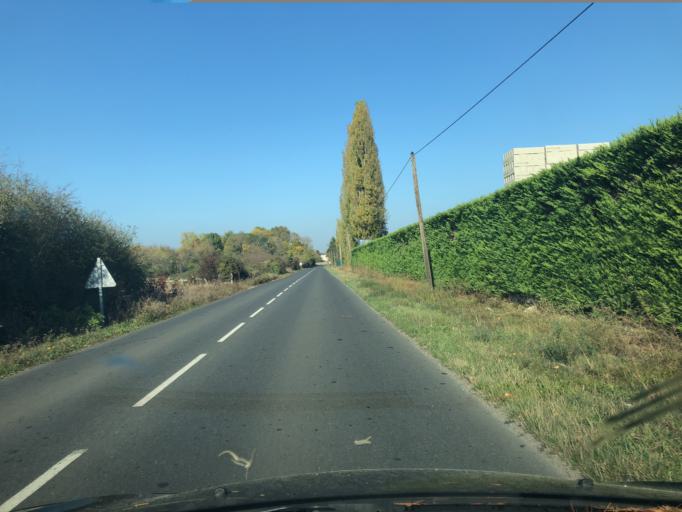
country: FR
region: Centre
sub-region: Departement d'Indre-et-Loire
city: Mettray
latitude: 47.4524
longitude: 0.6745
